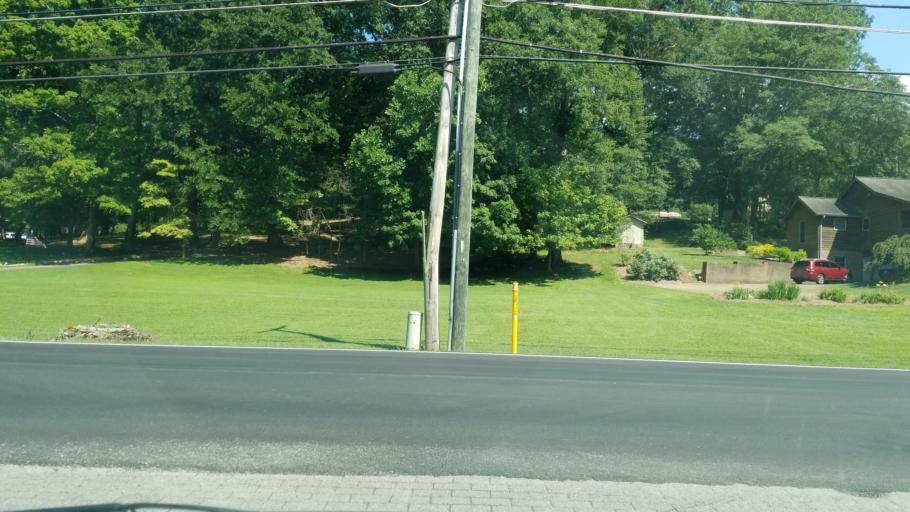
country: US
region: Tennessee
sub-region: Hamilton County
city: Middle Valley
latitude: 35.1355
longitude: -85.2107
